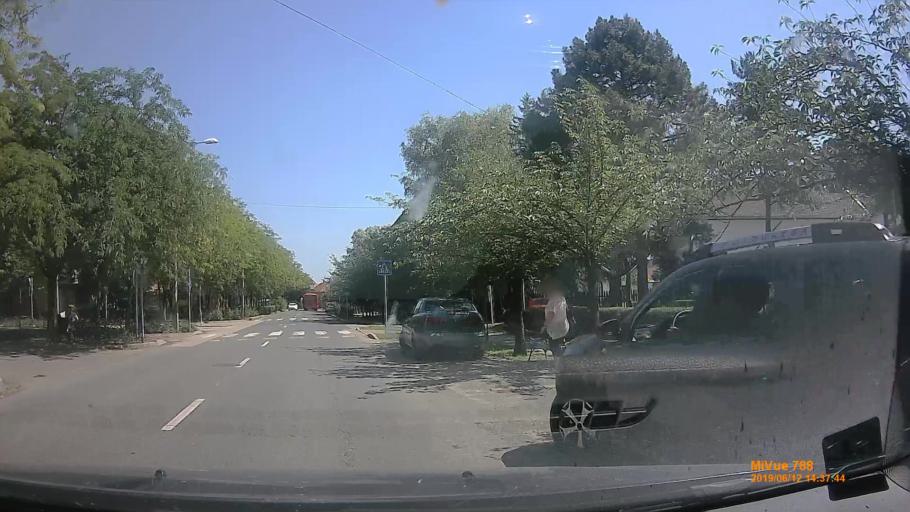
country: HU
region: Csongrad
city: Mako
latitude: 46.2119
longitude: 20.4737
